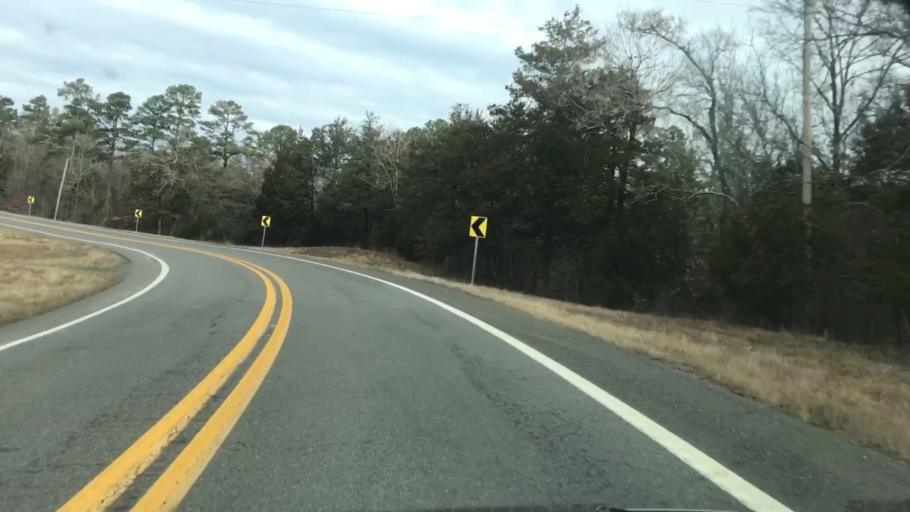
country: US
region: Arkansas
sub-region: Montgomery County
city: Mount Ida
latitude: 34.6189
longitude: -93.7039
